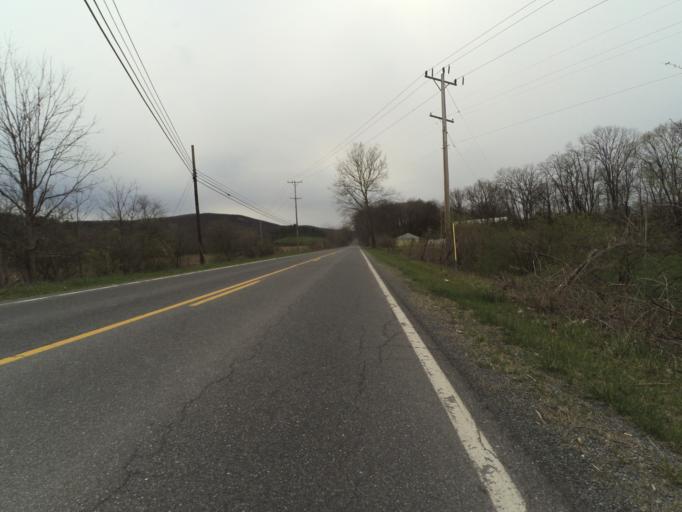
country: US
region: Pennsylvania
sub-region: Centre County
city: Milesburg
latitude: 40.9643
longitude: -77.7431
